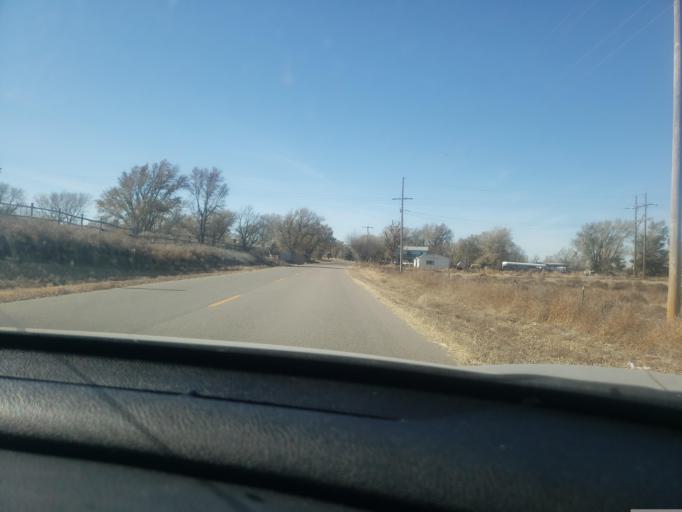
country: US
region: Kansas
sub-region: Finney County
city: Garden City
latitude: 37.9513
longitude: -100.8642
